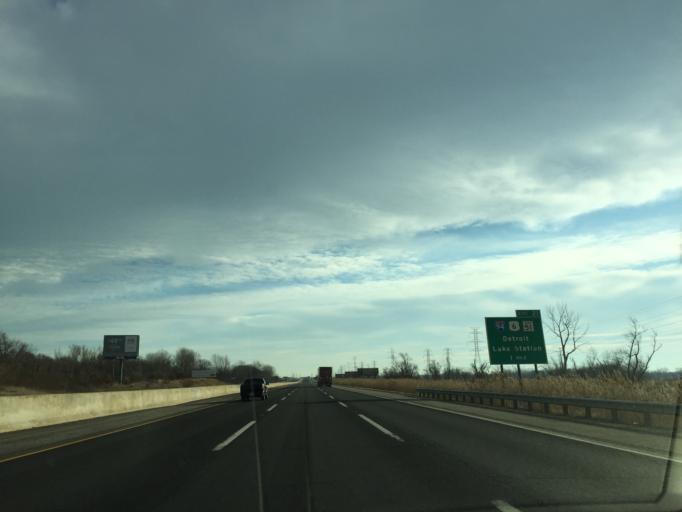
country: US
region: Indiana
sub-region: Lake County
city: Lake Station
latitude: 41.5903
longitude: -87.2637
